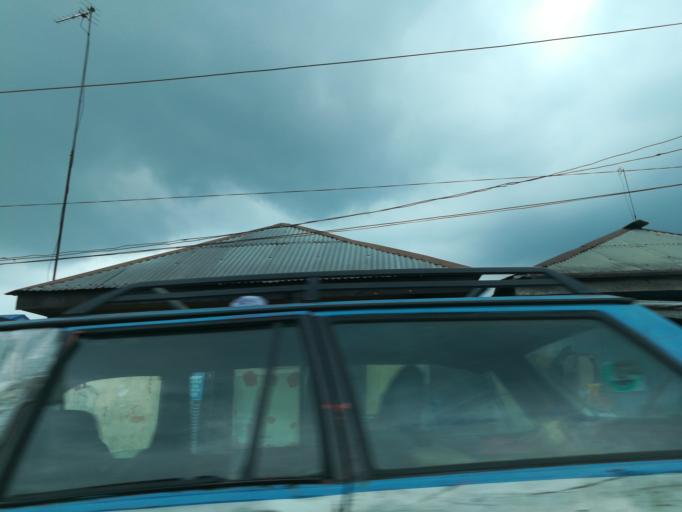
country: NG
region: Rivers
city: Port Harcourt
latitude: 4.7971
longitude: 6.9911
